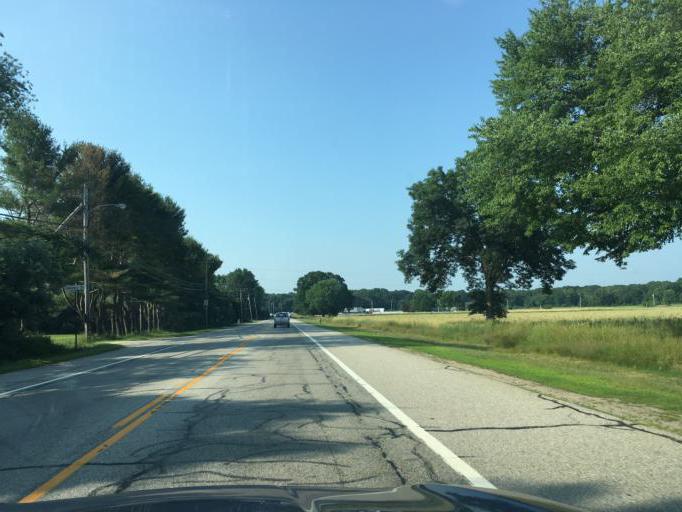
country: US
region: Rhode Island
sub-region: Washington County
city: Exeter
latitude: 41.5632
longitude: -71.5177
